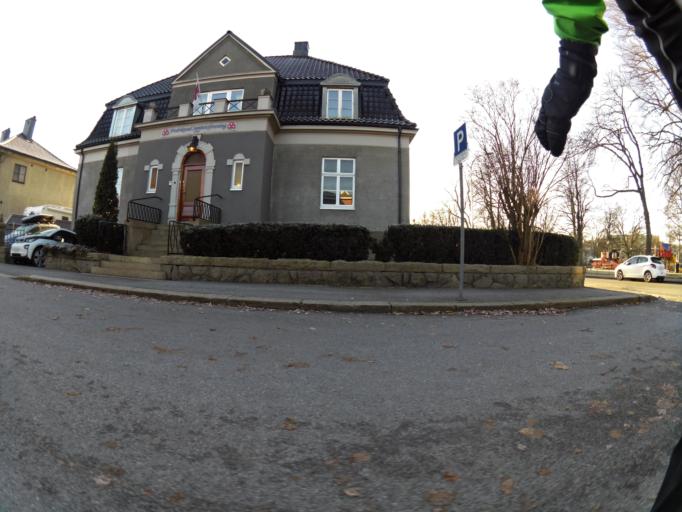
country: NO
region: Ostfold
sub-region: Fredrikstad
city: Fredrikstad
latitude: 59.2092
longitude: 10.9442
